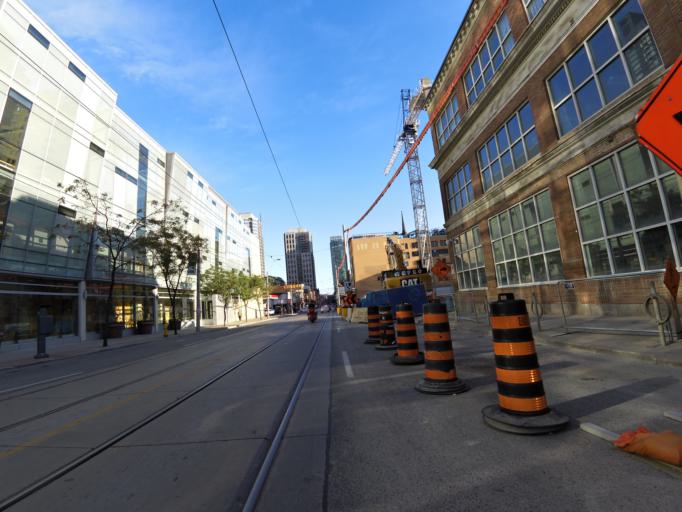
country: CA
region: Ontario
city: Toronto
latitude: 43.6576
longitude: -79.3776
